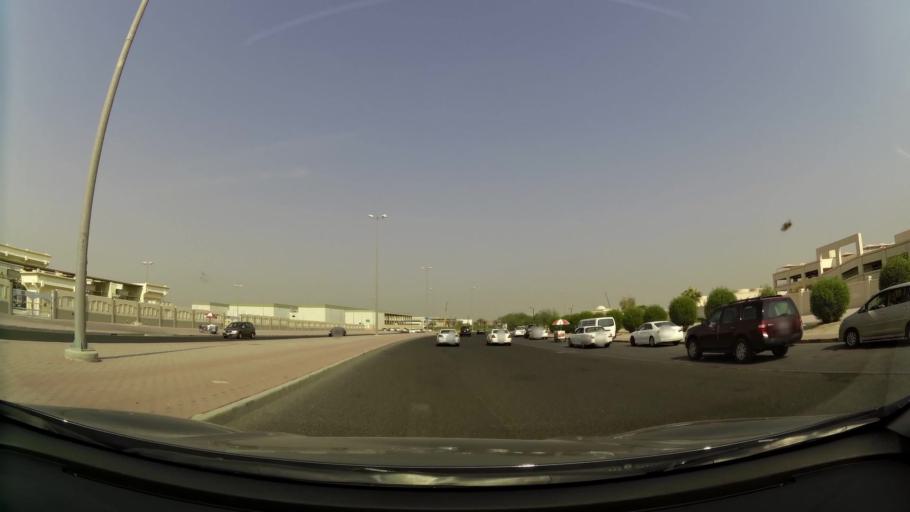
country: KW
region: Al Asimah
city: Ar Rabiyah
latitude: 29.2771
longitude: 47.9152
